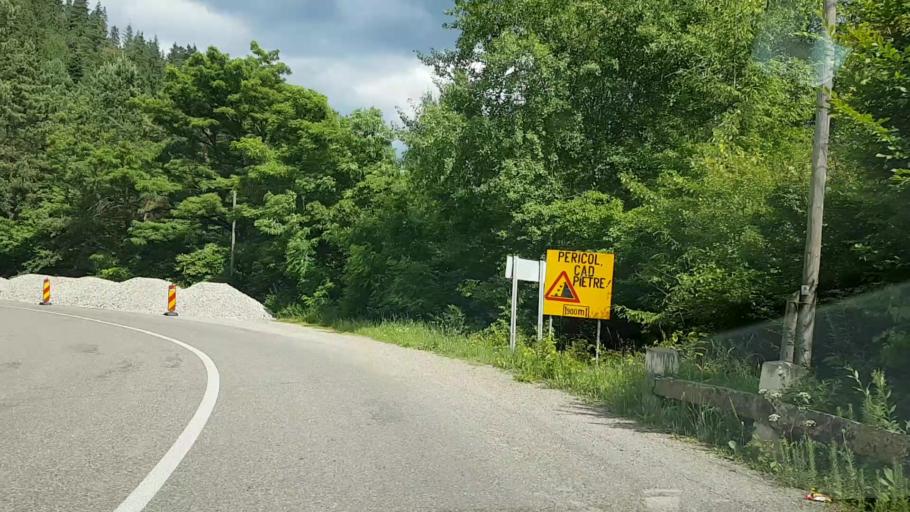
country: RO
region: Neamt
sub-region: Comuna Ceahlau
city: Ceahlau
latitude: 47.0528
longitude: 25.9797
